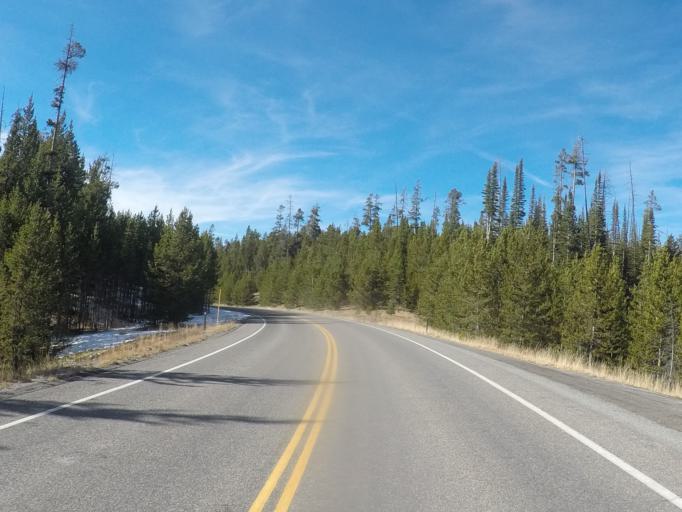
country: US
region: Montana
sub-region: Gallatin County
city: West Yellowstone
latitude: 44.5492
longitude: -110.4153
